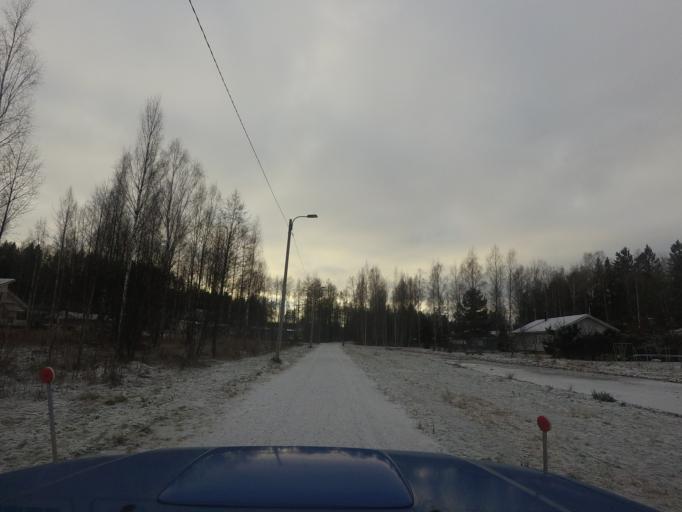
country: FI
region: Uusimaa
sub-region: Helsinki
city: Espoo
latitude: 60.1951
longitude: 24.6586
